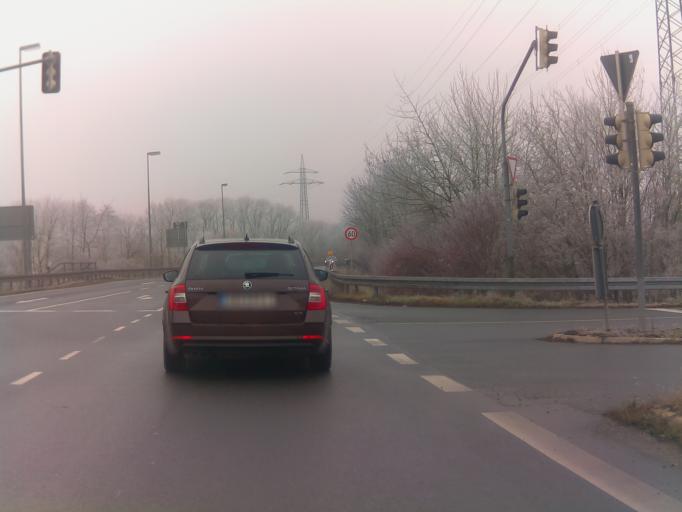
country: DE
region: Bavaria
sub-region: Regierungsbezirk Unterfranken
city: Kitzingen
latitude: 49.7317
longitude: 10.1744
